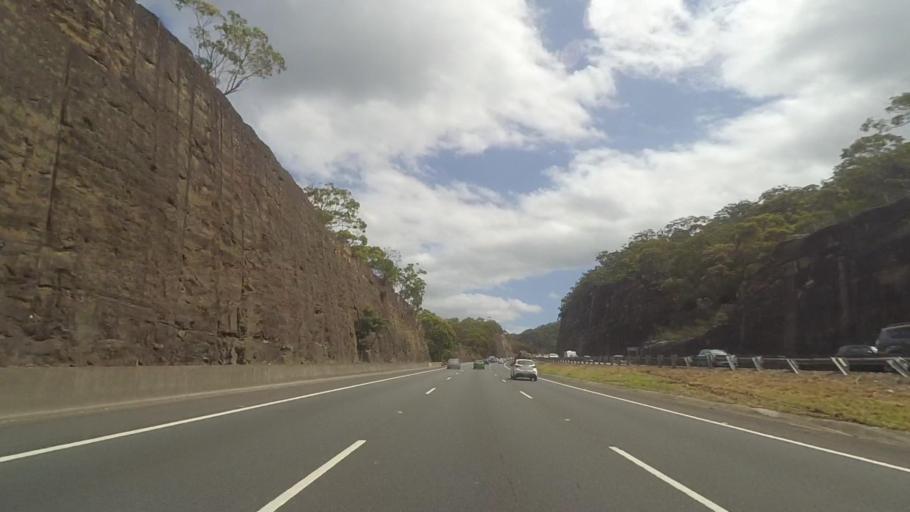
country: AU
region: New South Wales
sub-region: Hornsby Shire
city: Berowra
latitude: -33.5454
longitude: 151.1970
